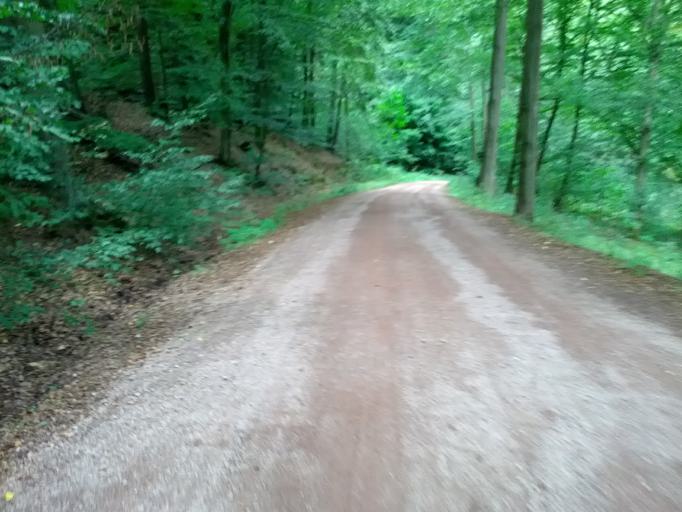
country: DE
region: Thuringia
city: Eisenach
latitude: 50.9517
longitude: 10.3081
